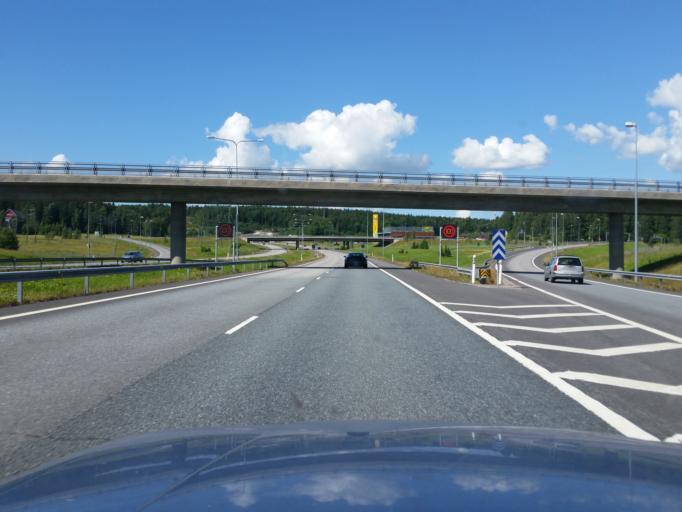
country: FI
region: Varsinais-Suomi
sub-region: Salo
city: Salo
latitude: 60.4161
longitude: 23.1739
